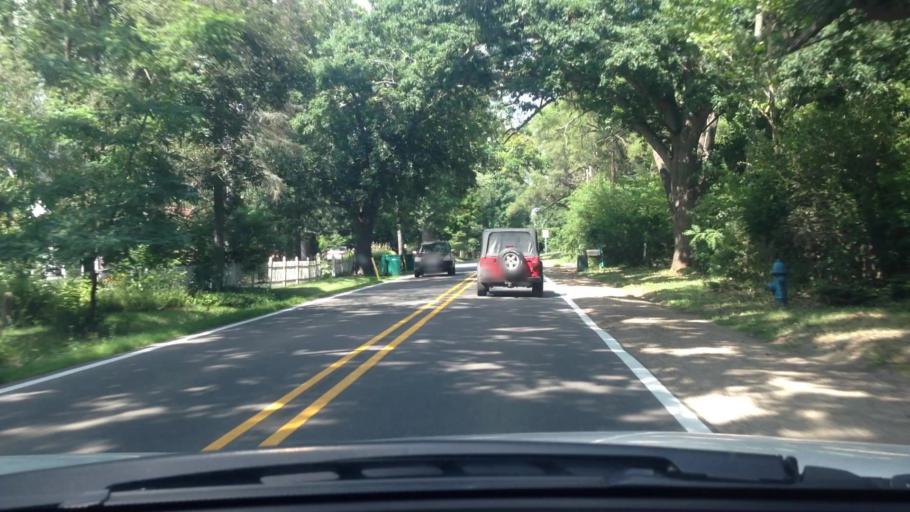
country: US
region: Michigan
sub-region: Oakland County
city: Pontiac
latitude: 42.6736
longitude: -83.3356
